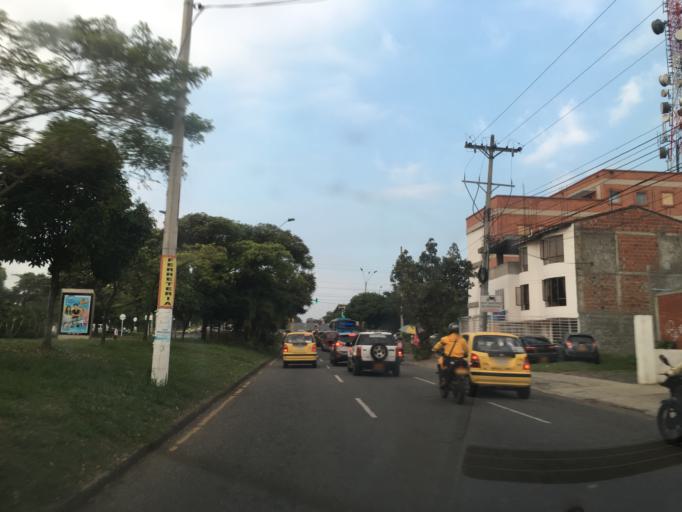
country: CO
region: Valle del Cauca
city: Cali
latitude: 3.3889
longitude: -76.5284
